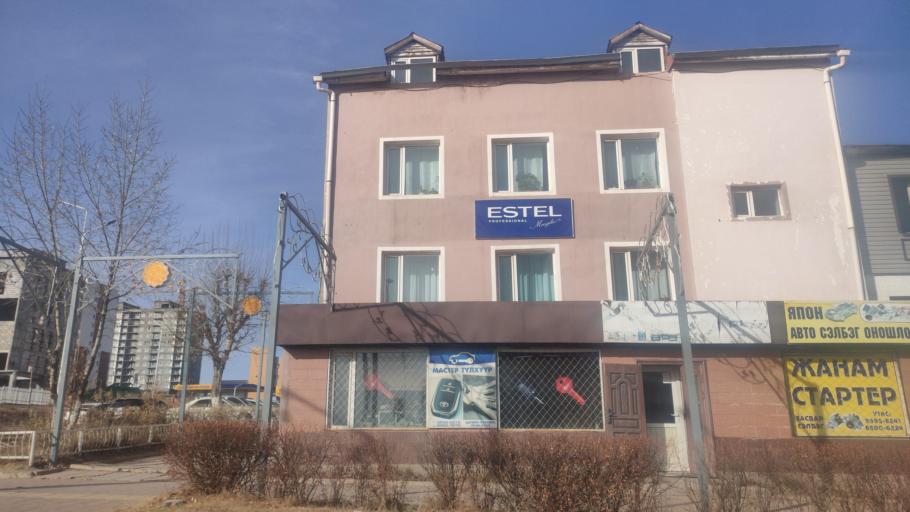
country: MN
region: Orhon
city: Erdenet
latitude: 49.0257
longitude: 104.0386
